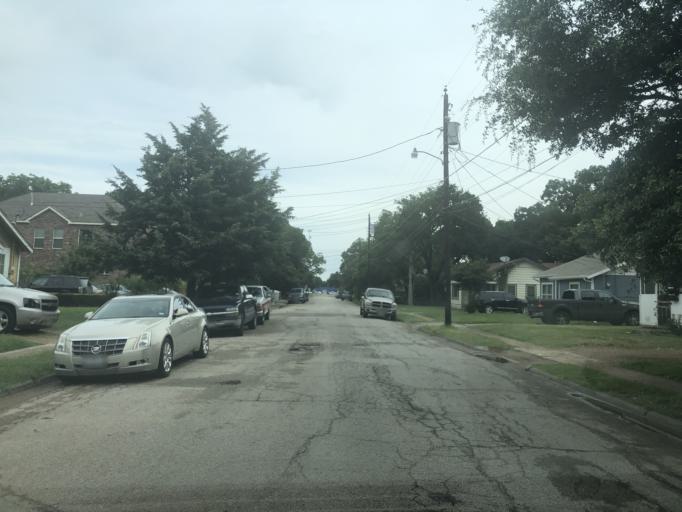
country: US
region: Texas
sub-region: Dallas County
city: Irving
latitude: 32.8108
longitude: -96.9403
